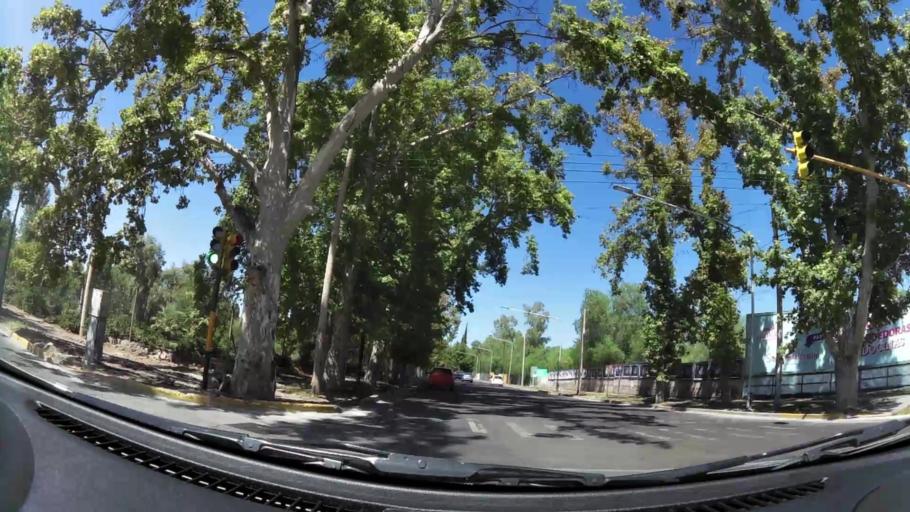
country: AR
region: Mendoza
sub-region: Departamento de Godoy Cruz
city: Godoy Cruz
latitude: -32.9070
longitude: -68.8662
